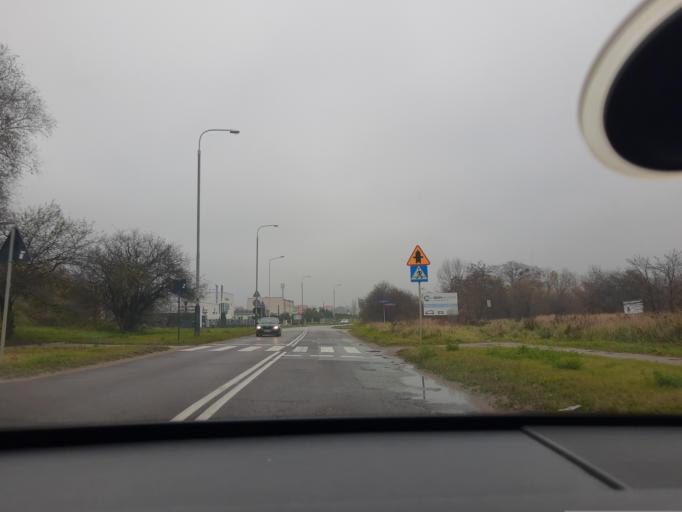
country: PL
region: Lodz Voivodeship
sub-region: Powiat pabianicki
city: Konstantynow Lodzki
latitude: 51.7359
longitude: 19.3797
